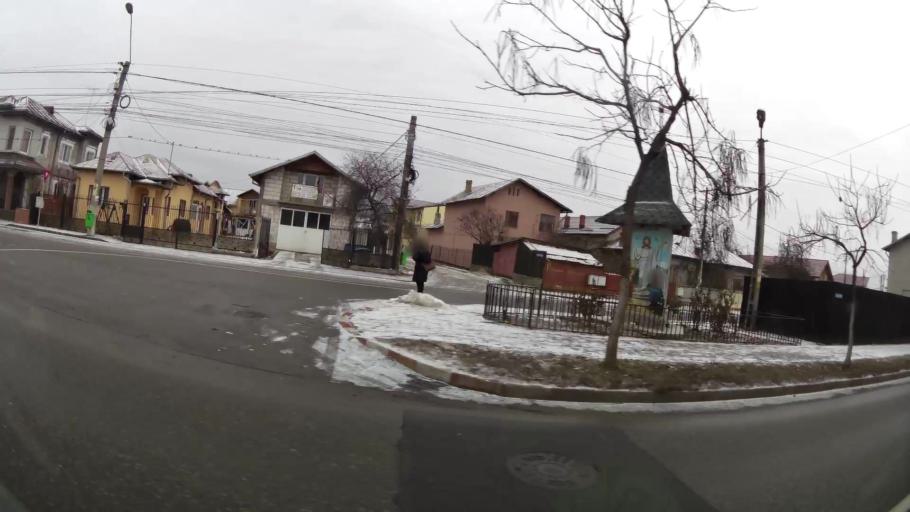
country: RO
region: Dambovita
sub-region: Comuna Ulmi
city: Ulmi
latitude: 44.9137
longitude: 25.4839
